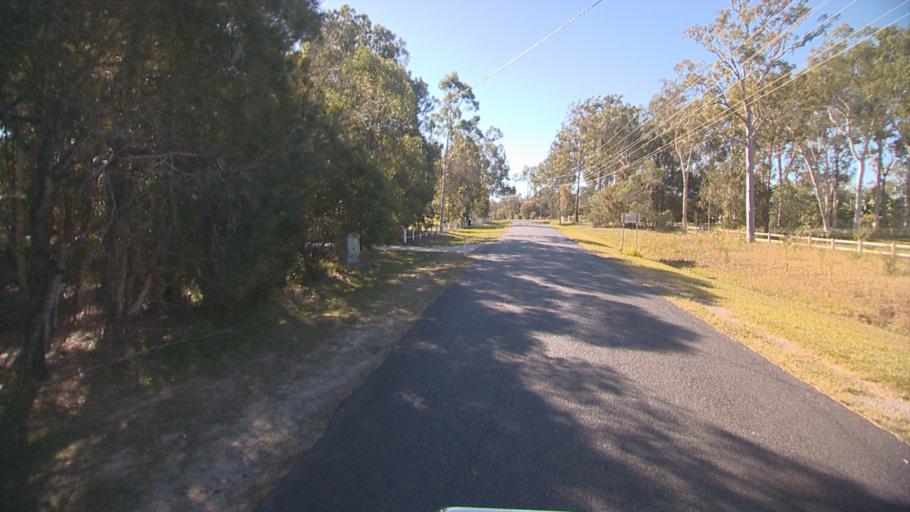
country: AU
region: Queensland
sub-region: Logan
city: Chambers Flat
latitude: -27.7334
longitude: 153.0716
